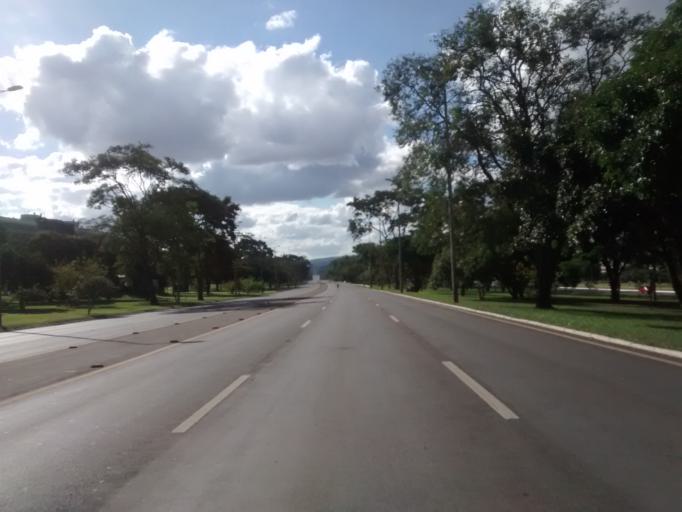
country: BR
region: Federal District
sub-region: Brasilia
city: Brasilia
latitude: -15.7678
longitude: -47.8824
